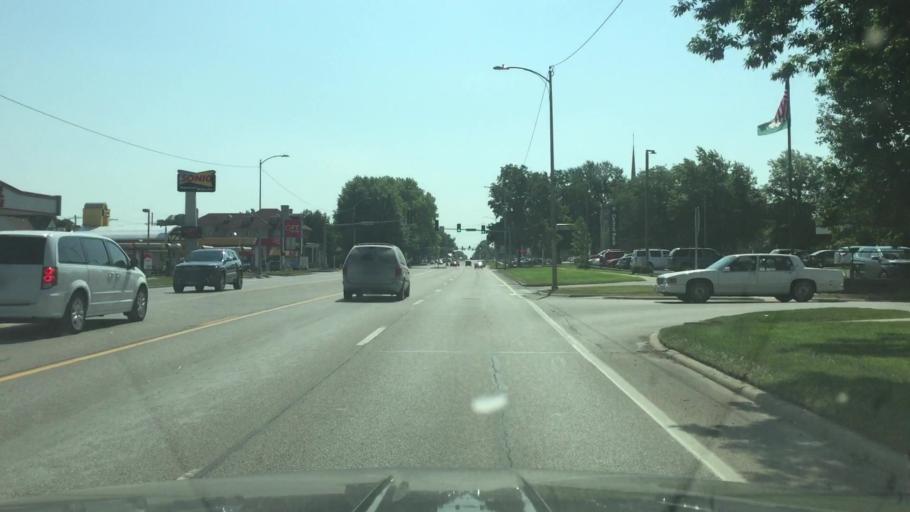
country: US
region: Missouri
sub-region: Pettis County
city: Sedalia
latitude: 38.7043
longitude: -93.2319
